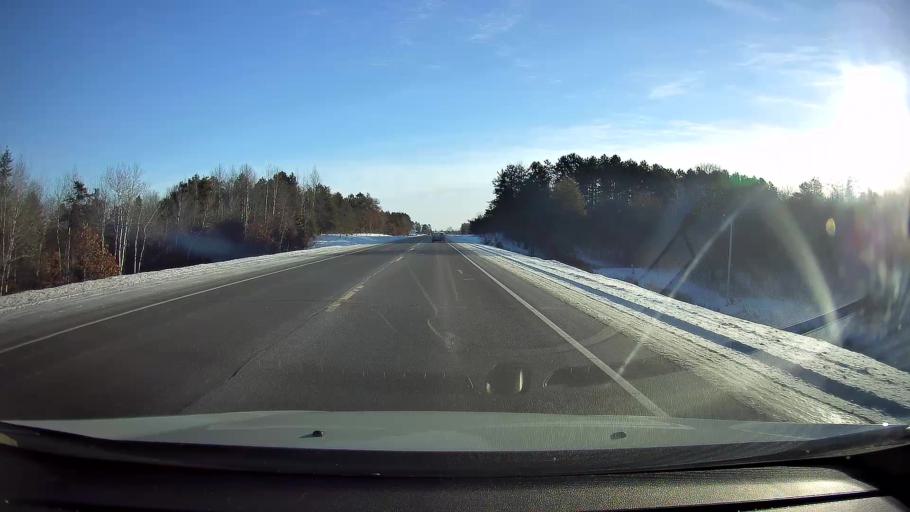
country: US
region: Wisconsin
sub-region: Washburn County
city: Spooner
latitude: 45.9104
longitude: -91.7756
